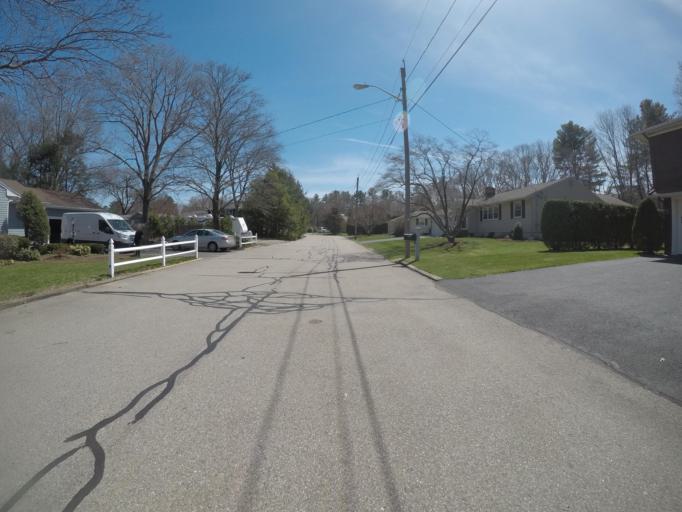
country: US
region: Massachusetts
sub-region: Bristol County
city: Easton
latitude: 42.0475
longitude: -71.0879
